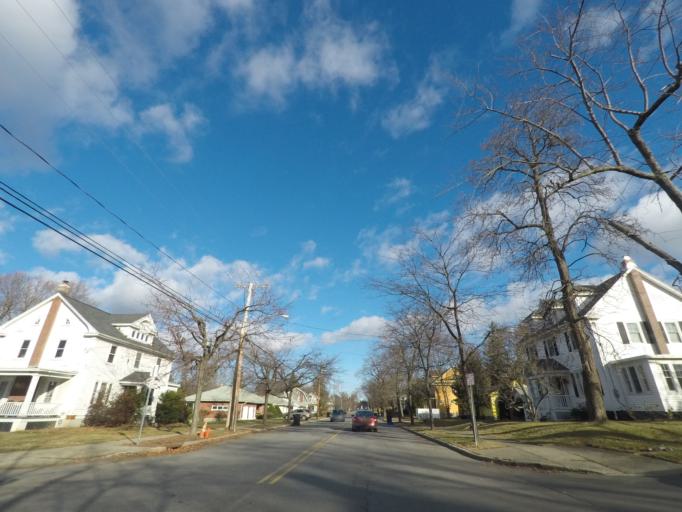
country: US
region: New York
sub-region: Albany County
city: Green Island
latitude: 42.7427
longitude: -73.6739
